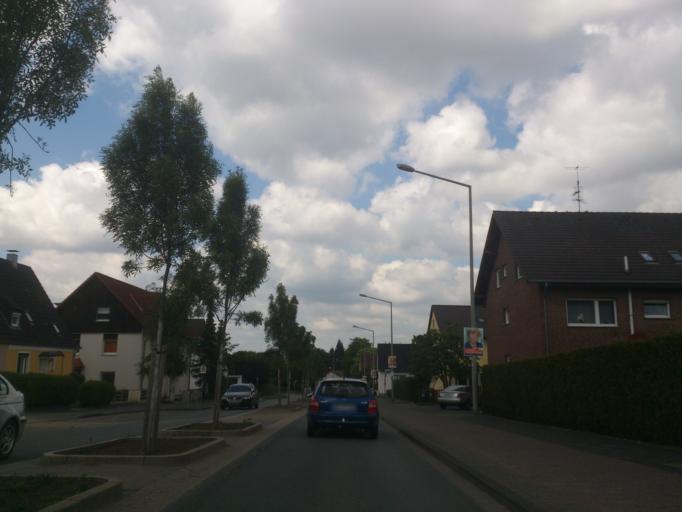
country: DE
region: North Rhine-Westphalia
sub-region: Regierungsbezirk Detmold
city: Paderborn
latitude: 51.7026
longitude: 8.7505
